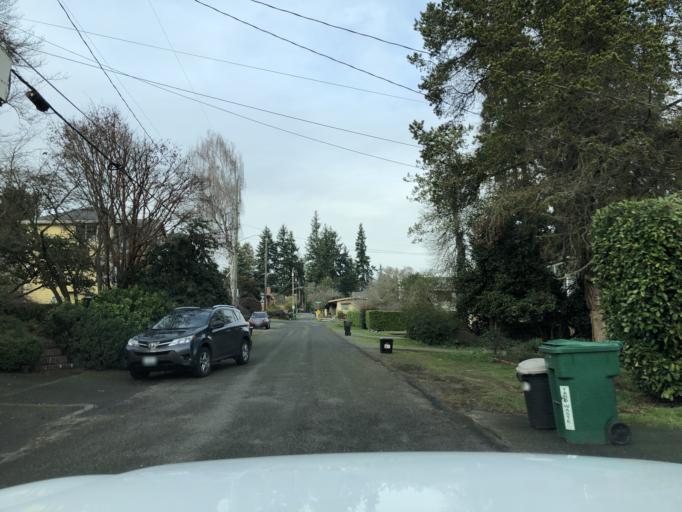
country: US
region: Washington
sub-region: King County
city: Inglewood-Finn Hill
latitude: 47.7084
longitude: -122.2786
